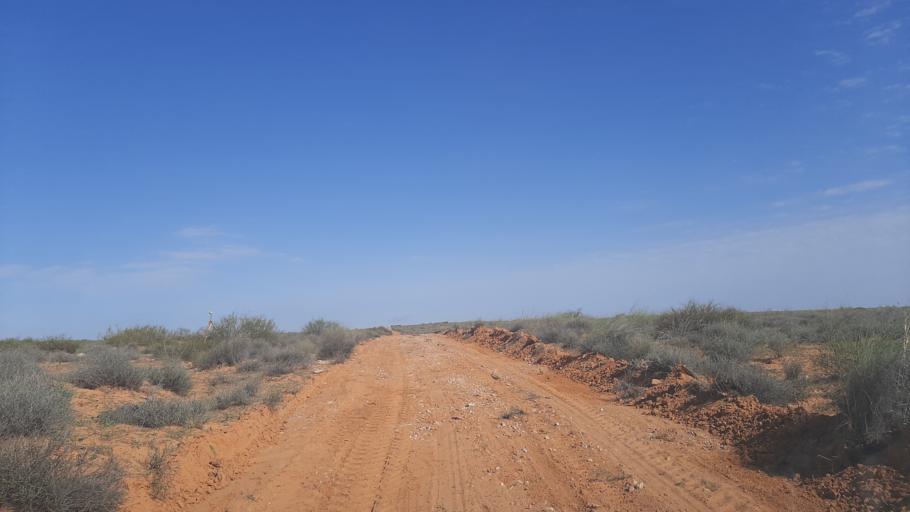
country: TN
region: Madanin
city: Medenine
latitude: 33.2474
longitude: 10.7461
